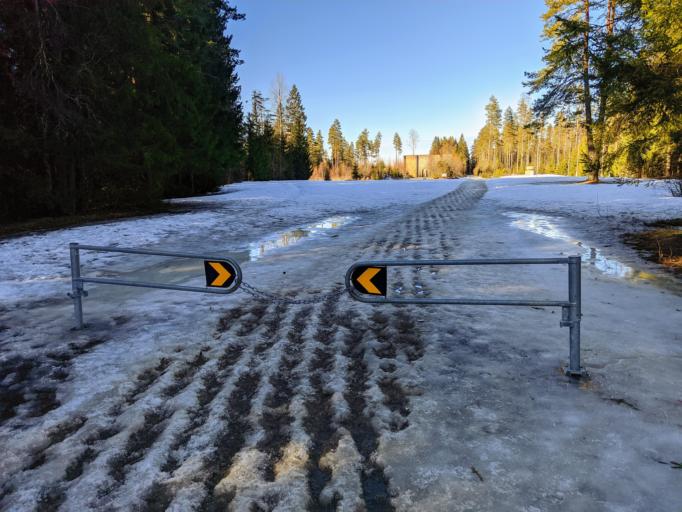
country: NO
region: Akershus
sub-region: Eidsvoll
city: Raholt
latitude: 60.2178
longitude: 11.1179
